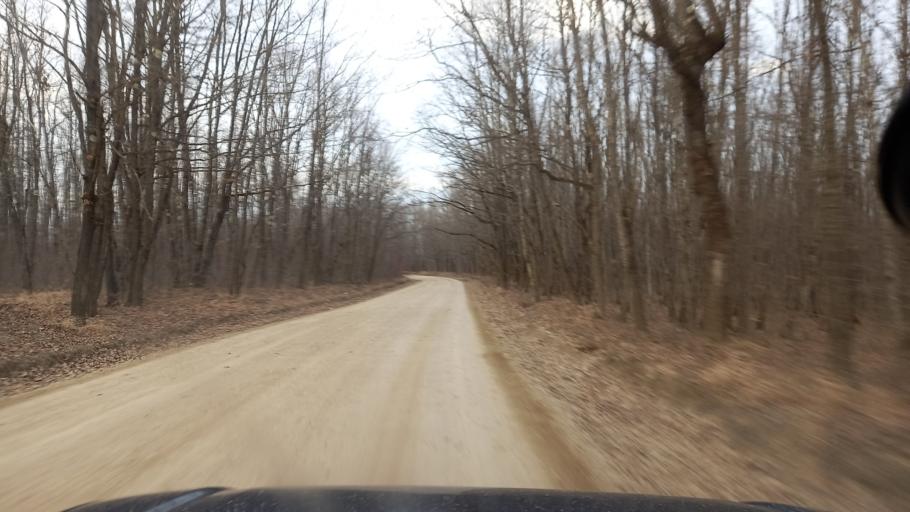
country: RU
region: Adygeya
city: Kamennomostskiy
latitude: 44.1526
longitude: 40.2470
